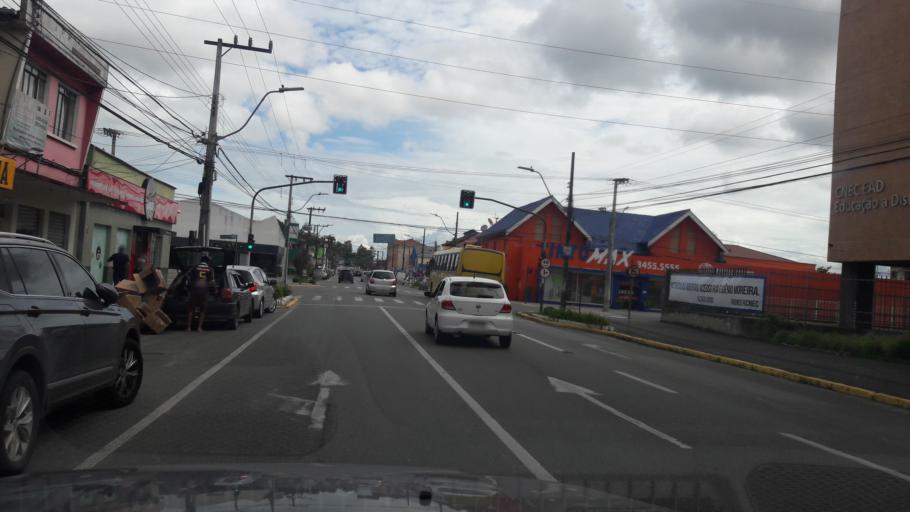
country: BR
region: Santa Catarina
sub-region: Joinville
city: Joinville
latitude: -26.3186
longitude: -48.8451
